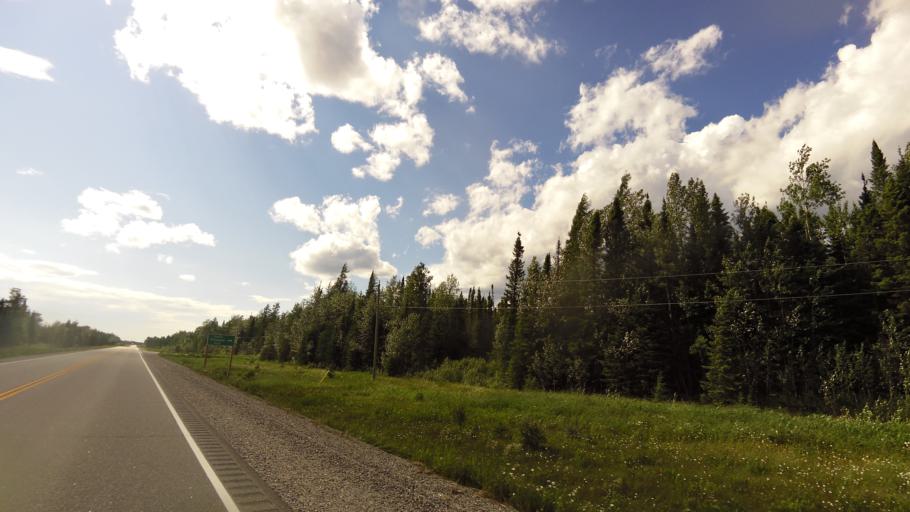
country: CA
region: Ontario
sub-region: Algoma
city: Hornepayne
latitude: 49.7736
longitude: -84.6138
